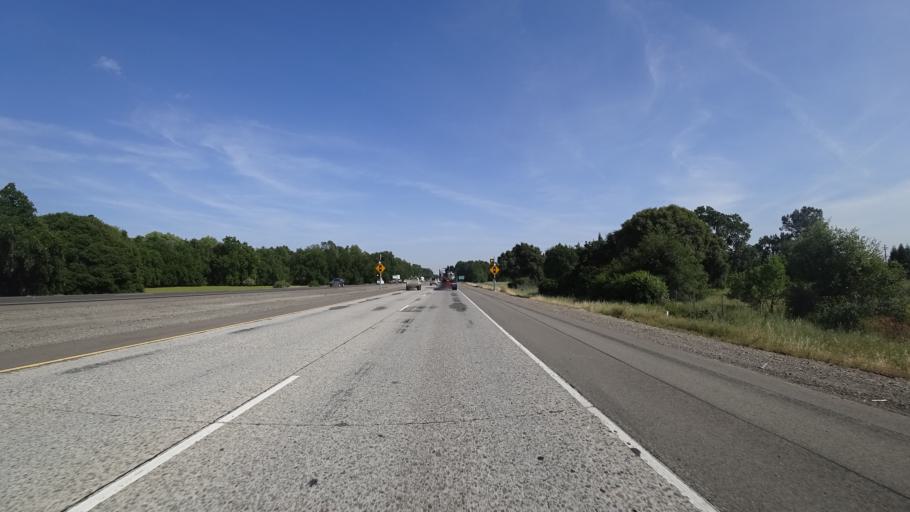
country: US
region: California
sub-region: Butte County
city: Durham
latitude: 39.6931
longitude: -121.7771
